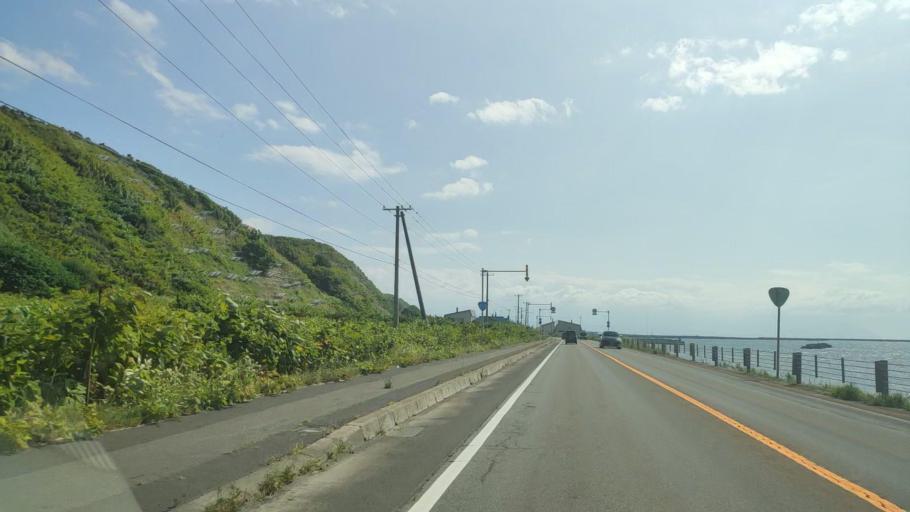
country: JP
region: Hokkaido
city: Rumoi
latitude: 43.9870
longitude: 141.6494
